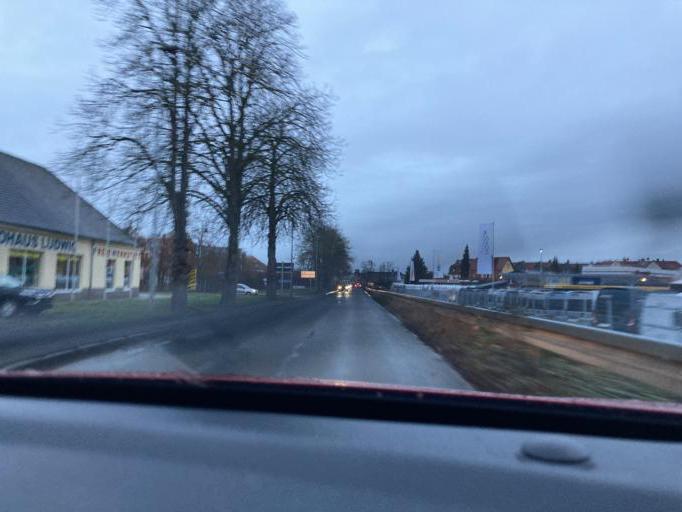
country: DE
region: Saxony-Anhalt
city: Naumburg
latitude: 51.1502
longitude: 11.8279
